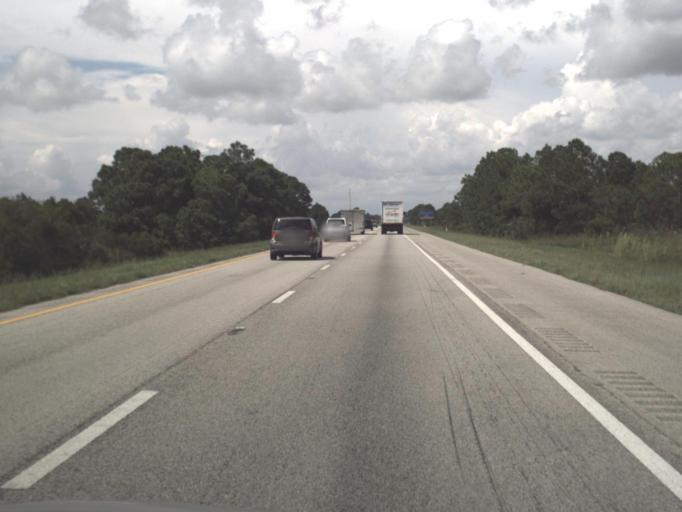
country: US
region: Florida
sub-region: Lee County
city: Burnt Store Marina
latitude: 26.8322
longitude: -81.9559
